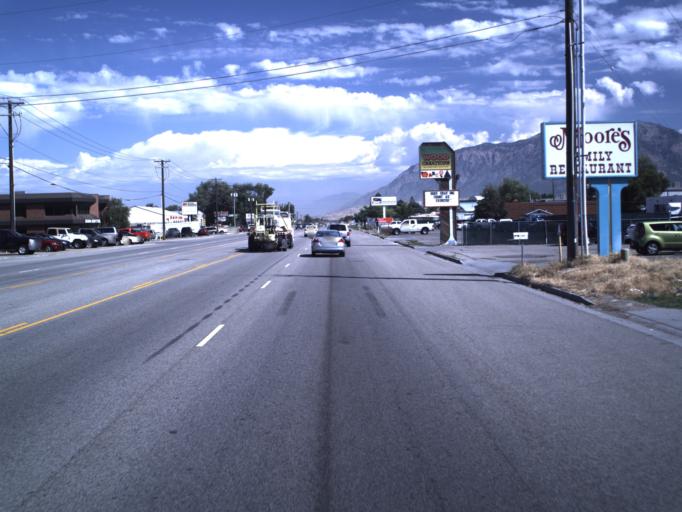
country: US
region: Utah
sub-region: Weber County
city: Marriott-Slaterville
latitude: 41.2213
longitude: -112.0256
